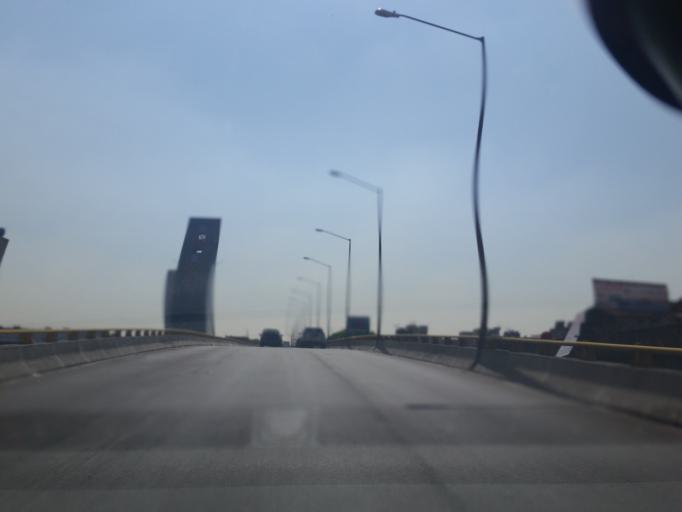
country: MX
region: Mexico City
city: Cuauhtemoc
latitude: 19.4547
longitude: -99.1567
